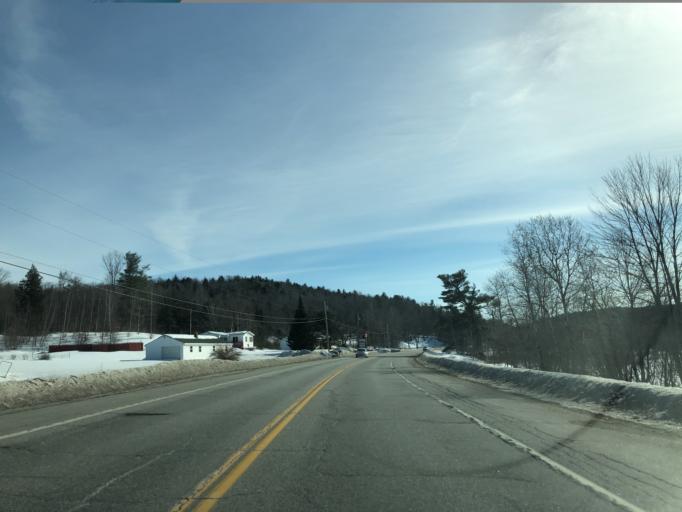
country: US
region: Maine
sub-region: Oxford County
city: West Paris
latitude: 44.3229
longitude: -70.5466
